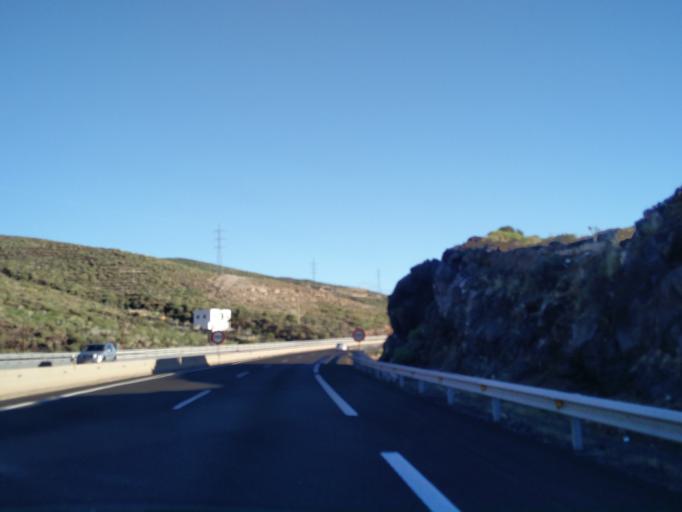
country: ES
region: Canary Islands
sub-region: Provincia de Santa Cruz de Tenerife
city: Fasnia
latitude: 28.2454
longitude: -16.4025
